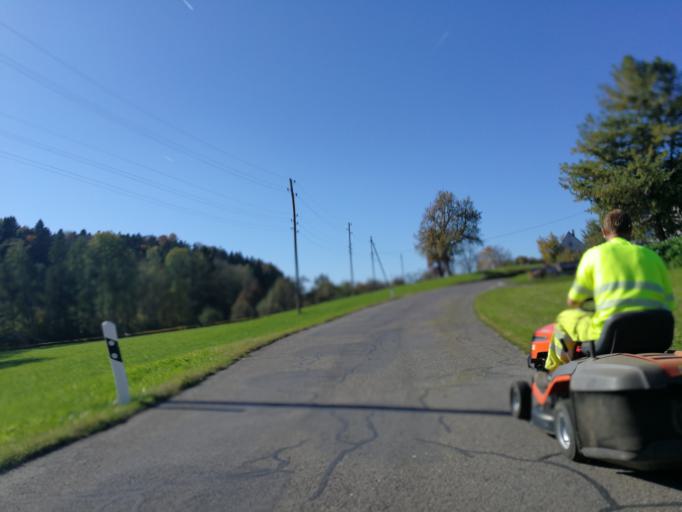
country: CH
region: Zurich
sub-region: Bezirk Hinwil
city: Binzikon
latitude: 47.2639
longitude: 8.7592
